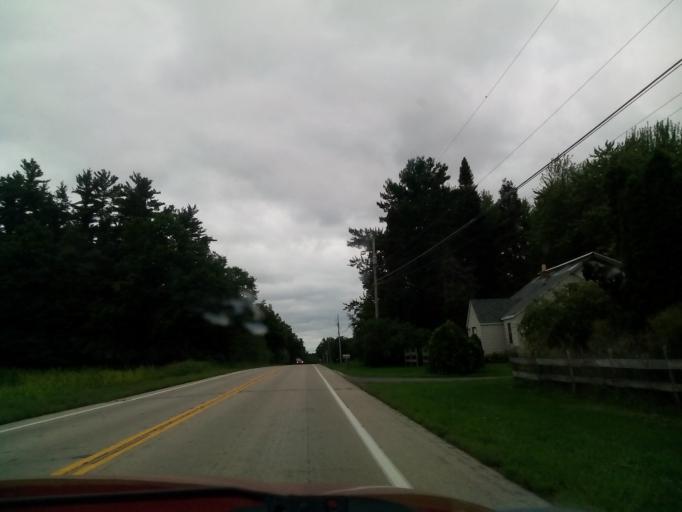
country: US
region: Wisconsin
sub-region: Outagamie County
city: Hortonville
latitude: 44.3596
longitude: -88.5911
